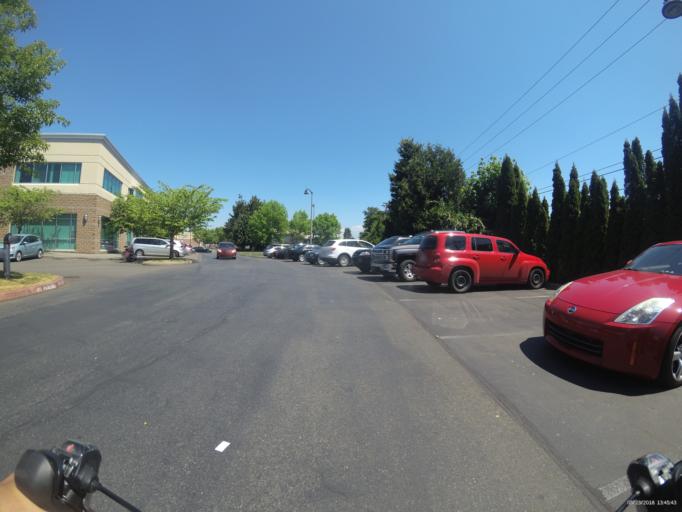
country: US
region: Washington
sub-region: Pierce County
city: Lakewood
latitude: 47.1608
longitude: -122.5162
